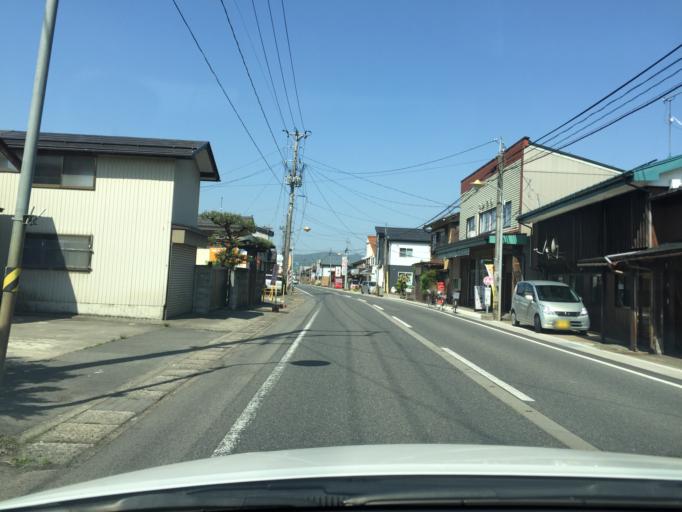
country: JP
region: Niigata
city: Muramatsu
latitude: 37.6884
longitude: 139.1708
